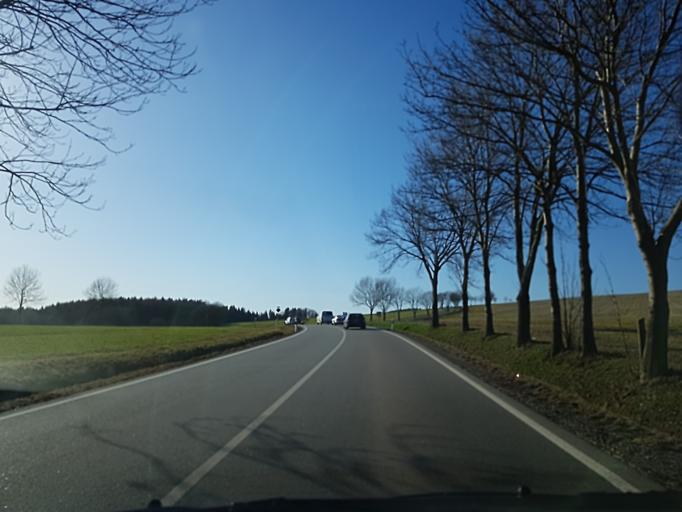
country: DE
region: Saxony
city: Oederan
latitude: 50.8623
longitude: 13.1474
